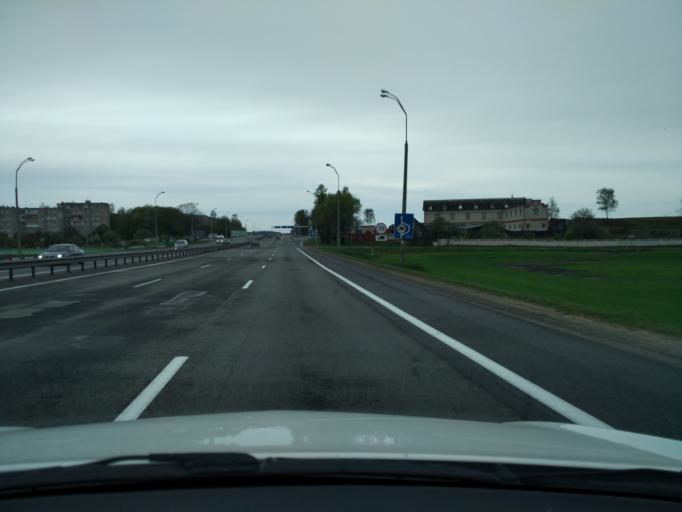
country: BY
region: Minsk
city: Pryvol'ny
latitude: 53.7976
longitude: 27.8089
